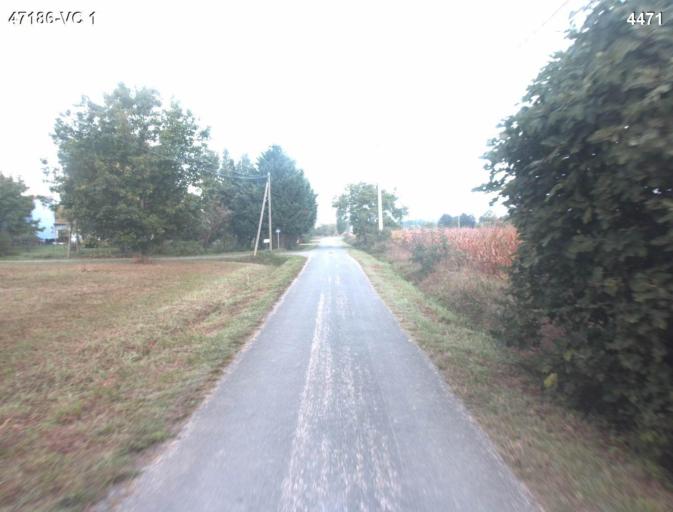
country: FR
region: Aquitaine
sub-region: Departement du Lot-et-Garonne
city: Port-Sainte-Marie
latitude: 44.2250
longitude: 0.4401
